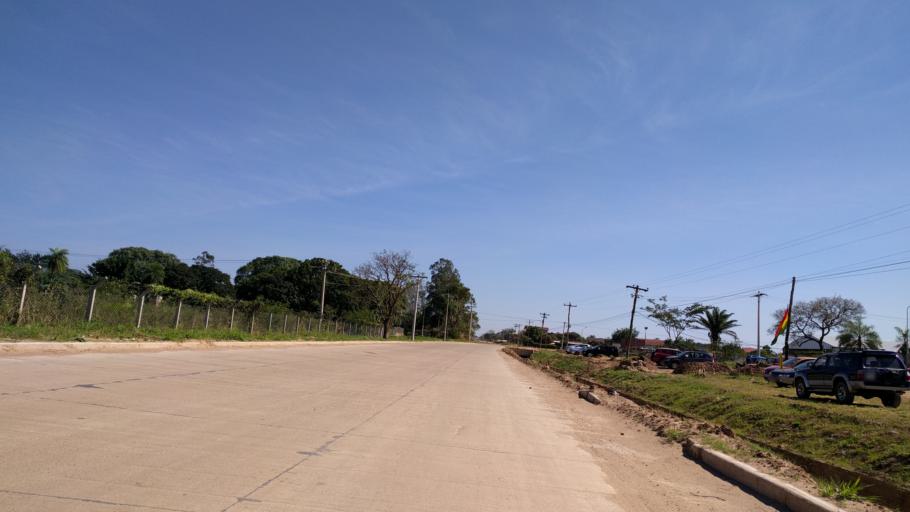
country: BO
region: Santa Cruz
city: Santa Cruz de la Sierra
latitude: -17.8457
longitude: -63.2277
